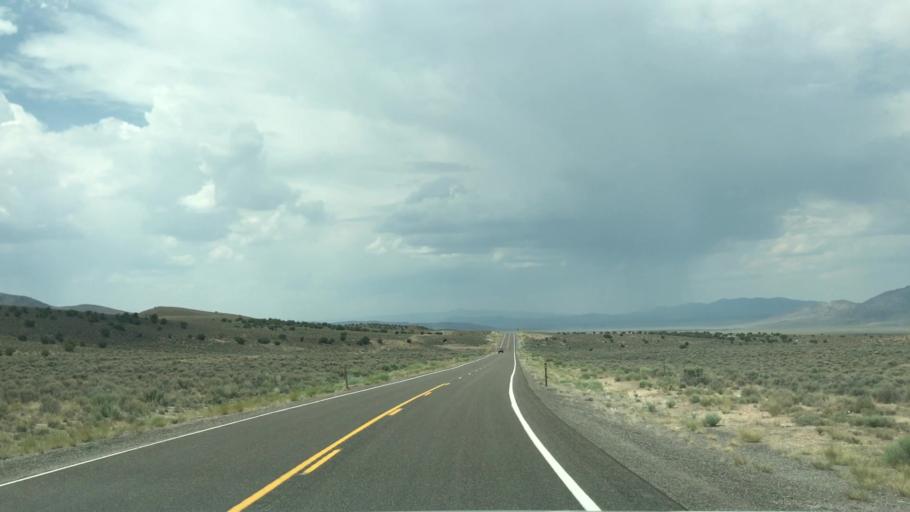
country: US
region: Nevada
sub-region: Eureka County
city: Eureka
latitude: 39.3981
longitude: -115.7126
